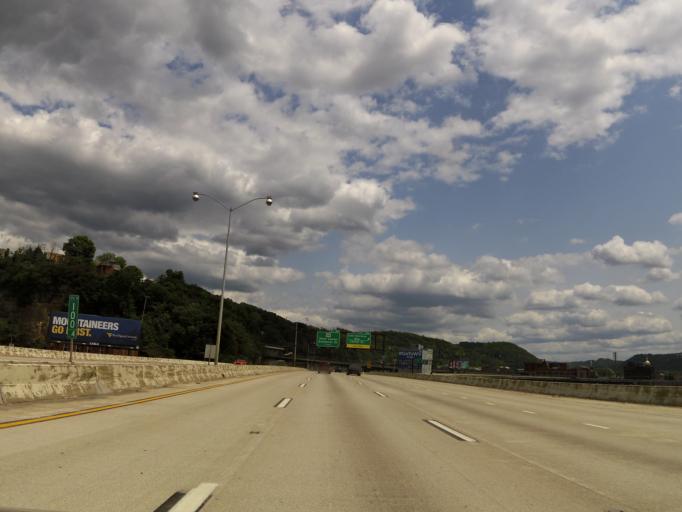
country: US
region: West Virginia
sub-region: Kanawha County
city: Charleston
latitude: 38.3535
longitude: -81.6293
